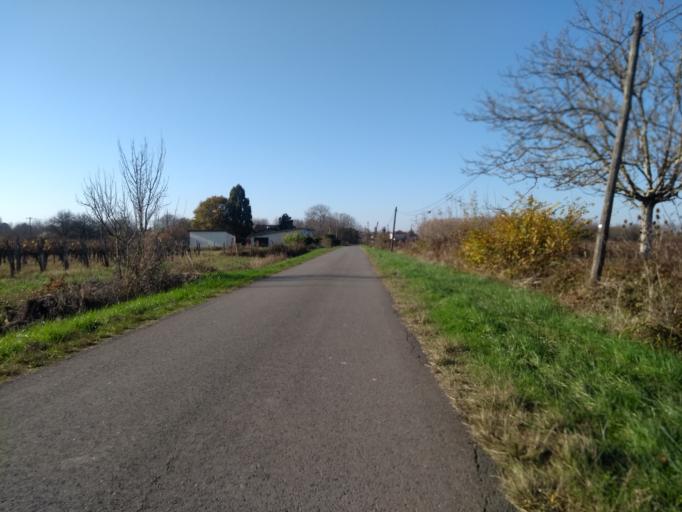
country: FR
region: Aquitaine
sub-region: Departement de la Gironde
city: Cambes
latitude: 44.7297
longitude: -0.4779
